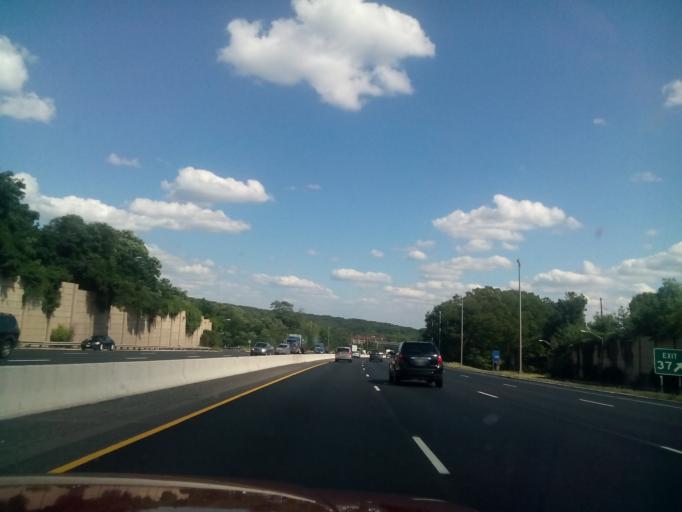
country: US
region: New Jersey
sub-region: Morris County
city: Rockaway
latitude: 40.9105
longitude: -74.5078
